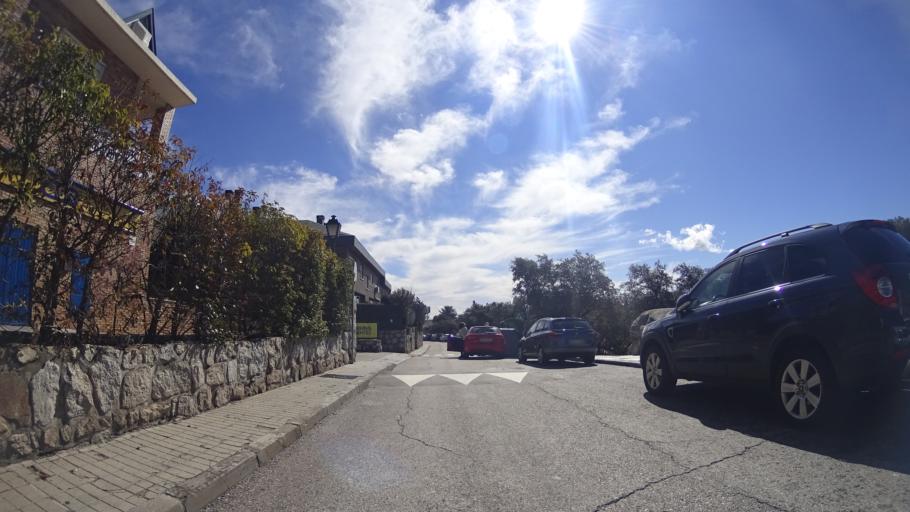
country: ES
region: Madrid
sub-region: Provincia de Madrid
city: Torrelodones
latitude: 40.5771
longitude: -3.9253
